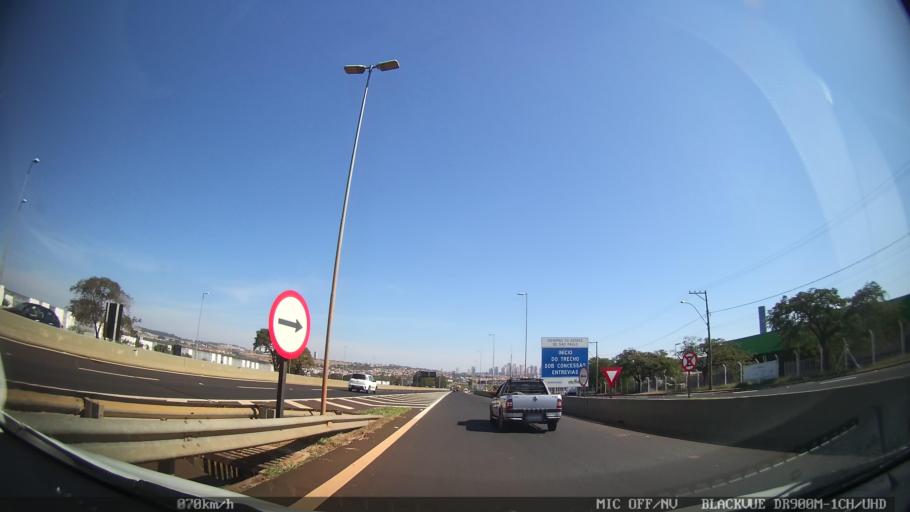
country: BR
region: Sao Paulo
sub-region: Ribeirao Preto
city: Ribeirao Preto
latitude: -21.2076
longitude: -47.7624
